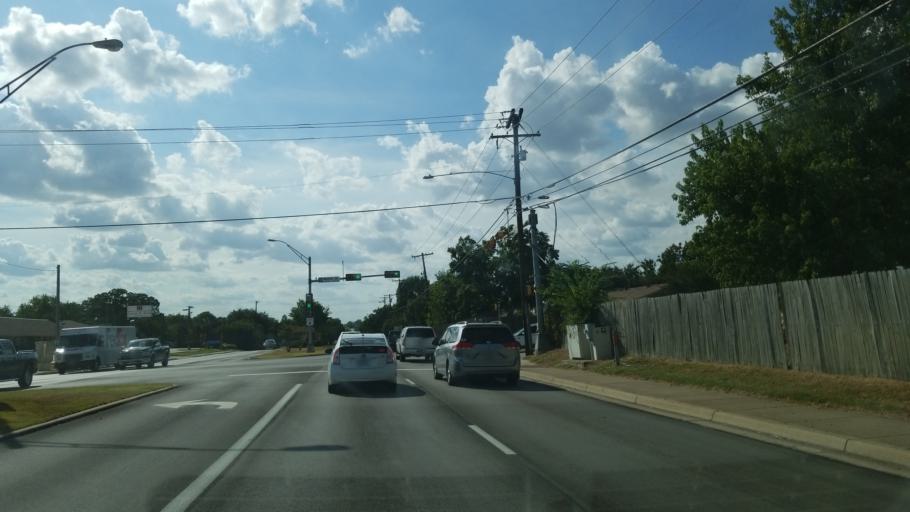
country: US
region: Texas
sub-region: Tarrant County
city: Bedford
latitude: 32.8521
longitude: -97.1240
